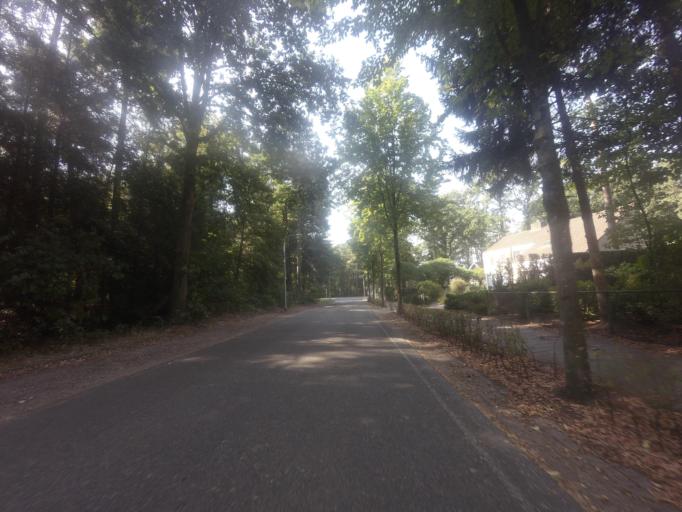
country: NL
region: North Brabant
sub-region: Gemeente Goirle
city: Goirle
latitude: 51.5700
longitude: 5.0319
